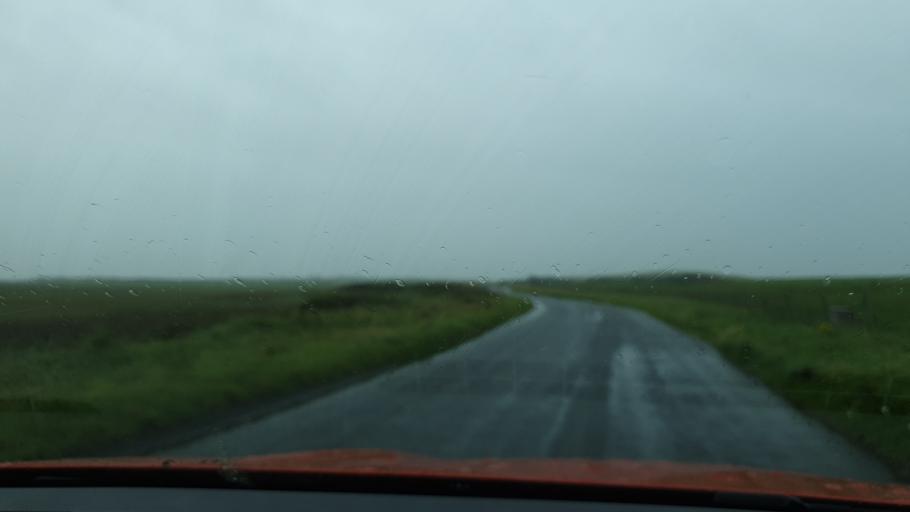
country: GB
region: England
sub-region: Cumbria
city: Barrow in Furness
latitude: 54.0695
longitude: -3.2264
